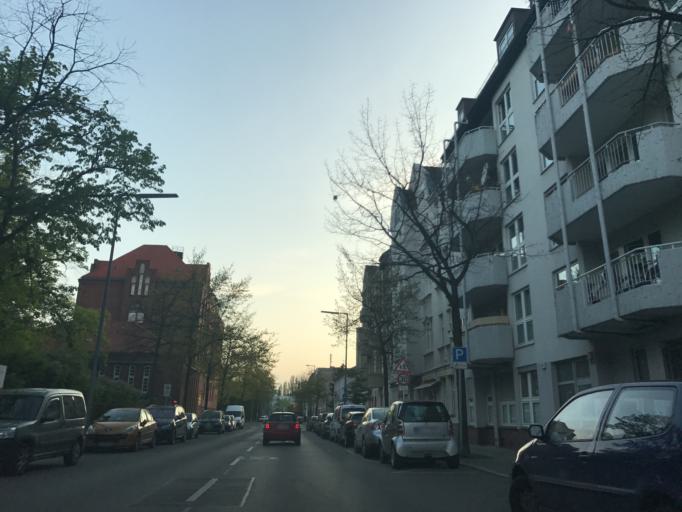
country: DE
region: Berlin
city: Wilhelmstadt
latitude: 52.5262
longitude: 13.1814
